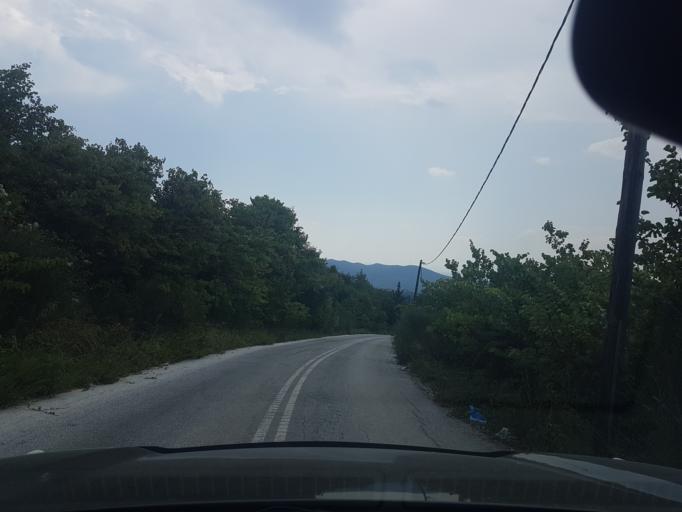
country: GR
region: Central Greece
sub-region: Nomos Evvoias
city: Kymi
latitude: 38.6389
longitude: 24.0668
